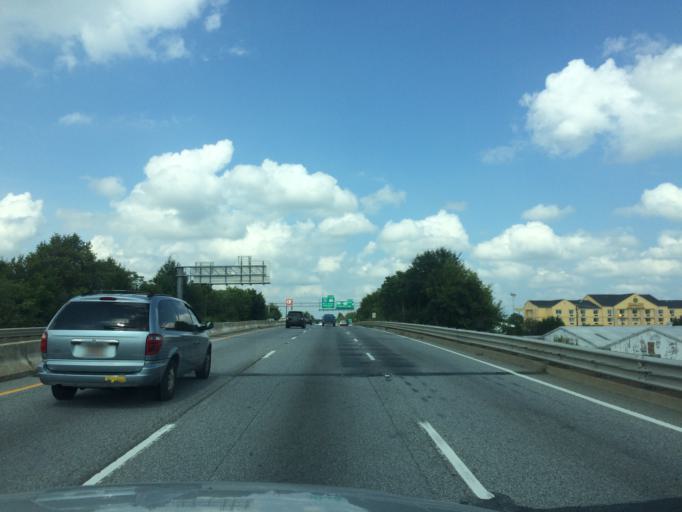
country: US
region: South Carolina
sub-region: Spartanburg County
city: Southern Shops
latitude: 34.9810
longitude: -81.9766
